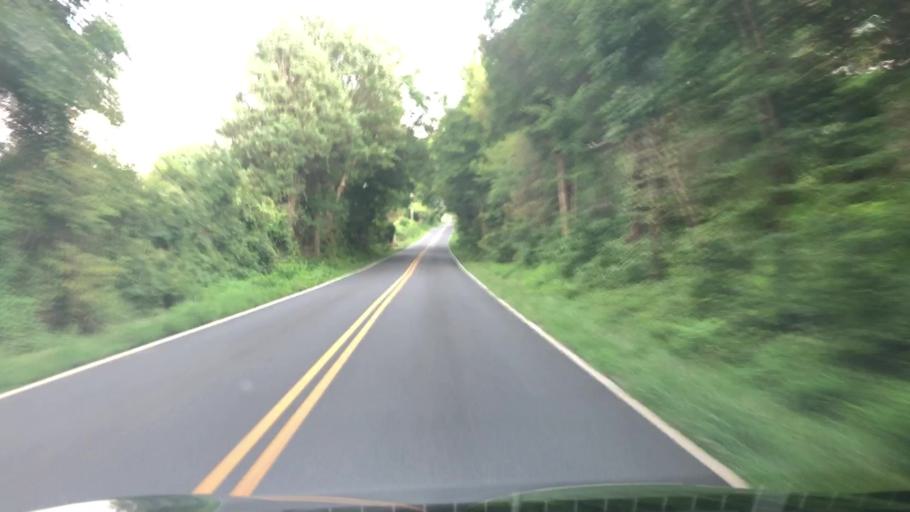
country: US
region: Virginia
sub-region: Fauquier County
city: Bealeton
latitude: 38.6012
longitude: -77.7166
